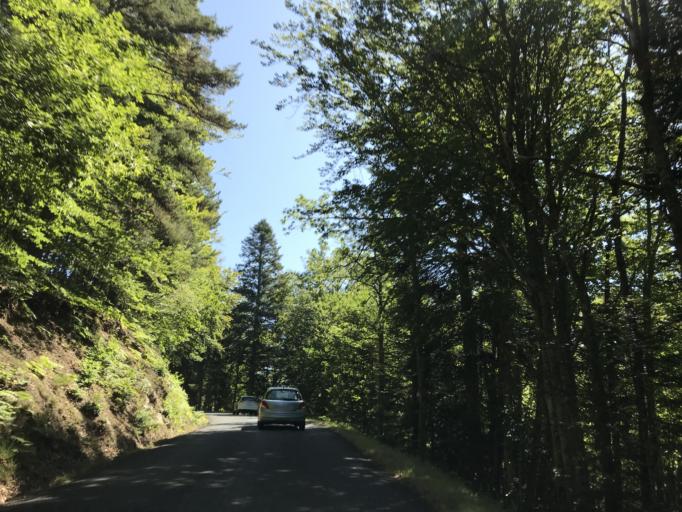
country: FR
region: Auvergne
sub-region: Departement du Puy-de-Dome
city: Job
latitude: 45.6696
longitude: 3.7433
